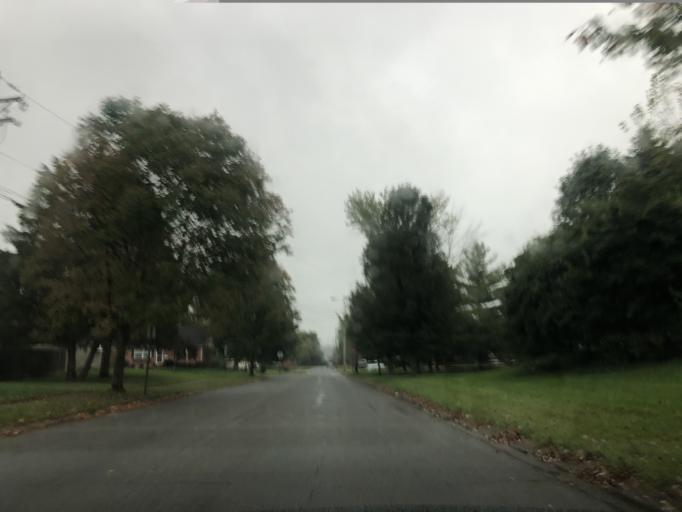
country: US
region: Ohio
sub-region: Hamilton County
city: The Village of Indian Hill
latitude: 39.2601
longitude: -84.2816
